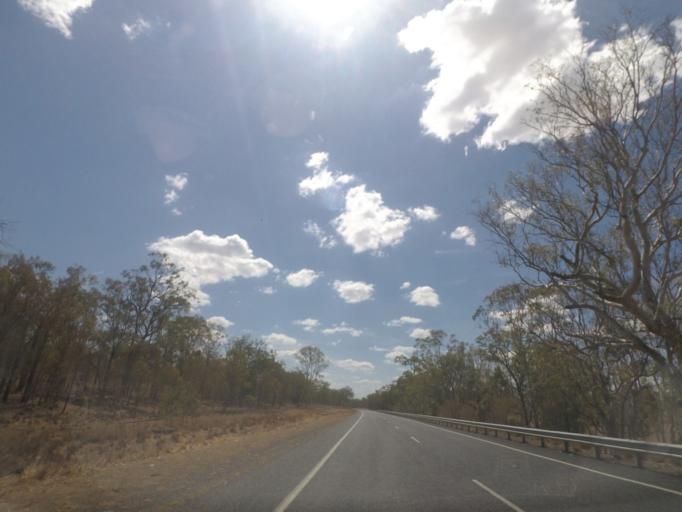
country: AU
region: Queensland
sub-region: Southern Downs
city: Warwick
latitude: -28.1664
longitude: 151.7248
